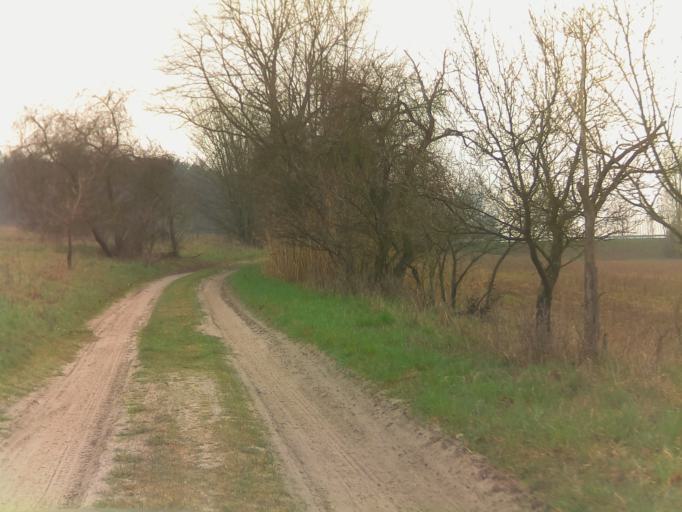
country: DE
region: Brandenburg
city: Lieberose
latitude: 52.0119
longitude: 14.2166
